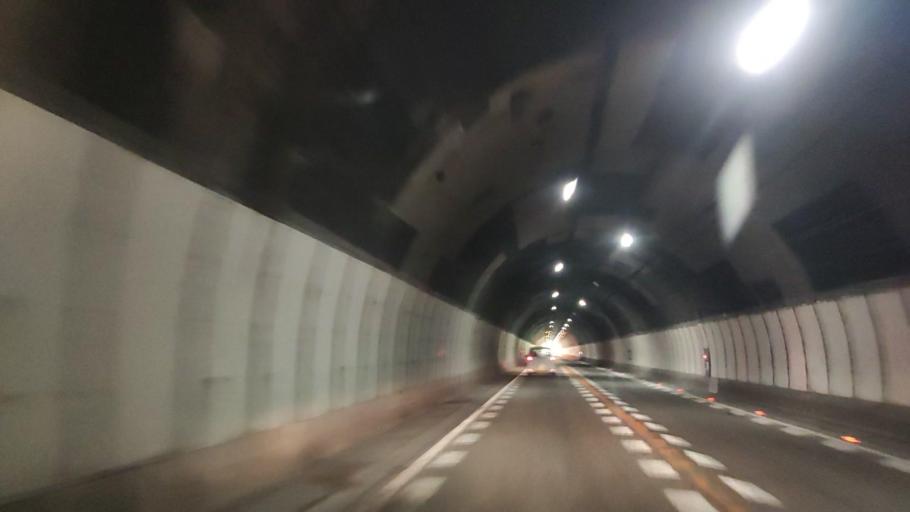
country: JP
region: Hyogo
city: Toyooka
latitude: 35.4839
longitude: 134.5795
